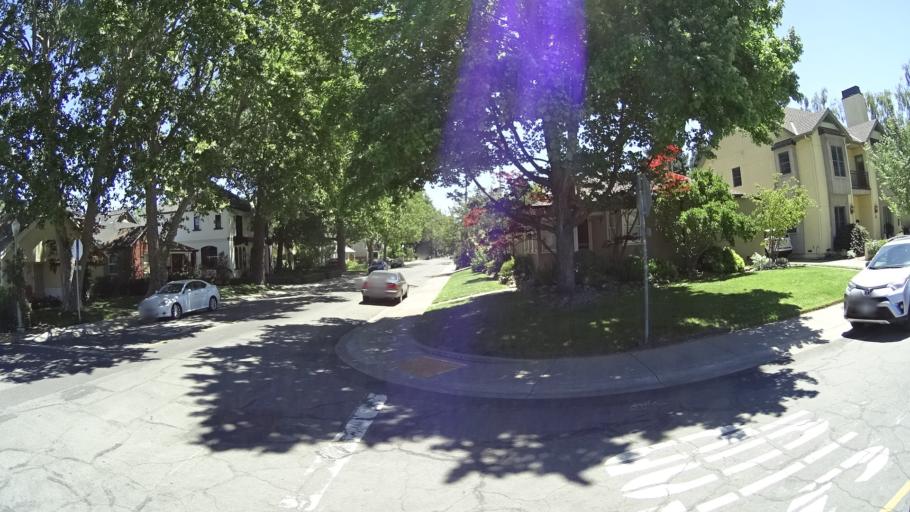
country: US
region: California
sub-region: Sacramento County
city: Sacramento
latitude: 38.5744
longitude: -121.4441
